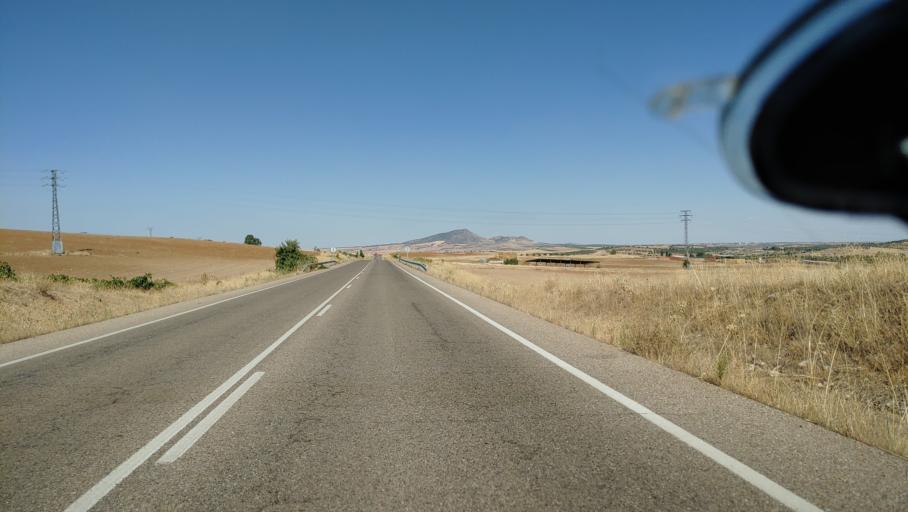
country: ES
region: Castille-La Mancha
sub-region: Province of Toledo
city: Pulgar
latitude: 39.6818
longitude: -4.1739
